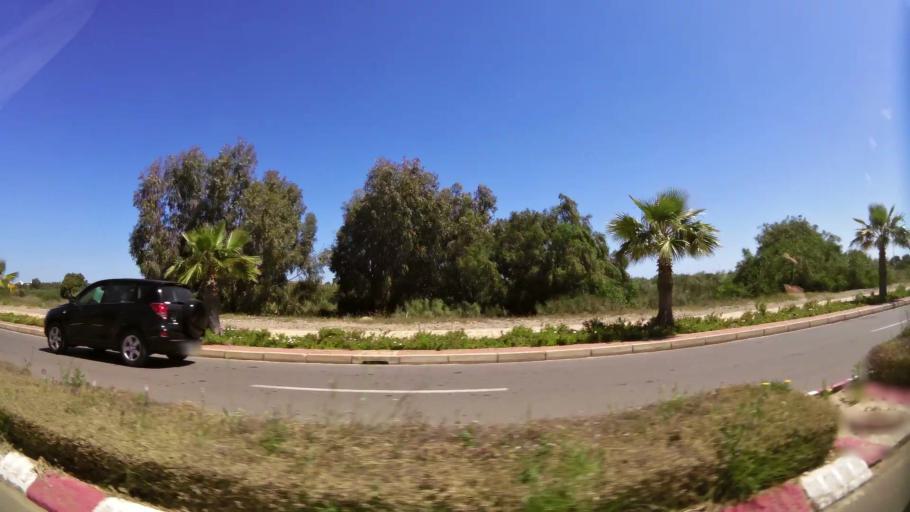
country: MA
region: Oriental
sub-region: Berkane-Taourirt
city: Madagh
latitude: 35.0964
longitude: -2.2756
